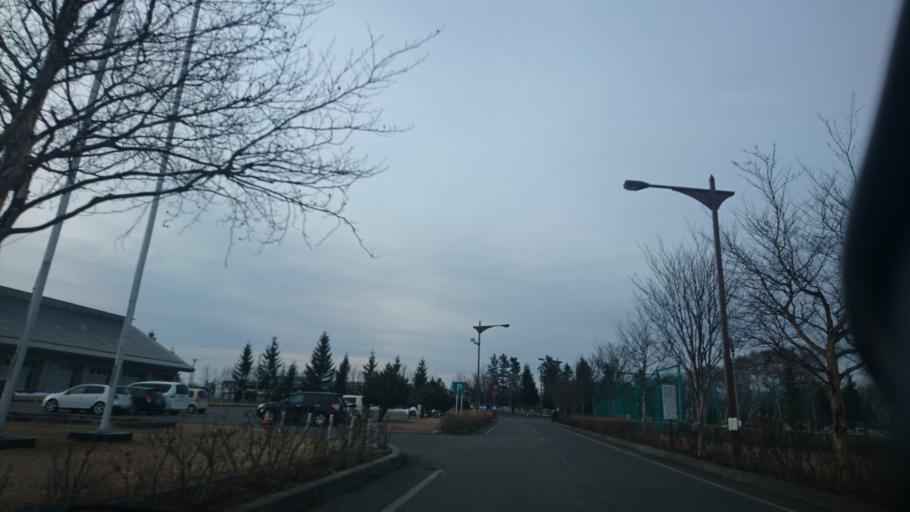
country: JP
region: Hokkaido
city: Otofuke
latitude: 42.9927
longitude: 143.1946
